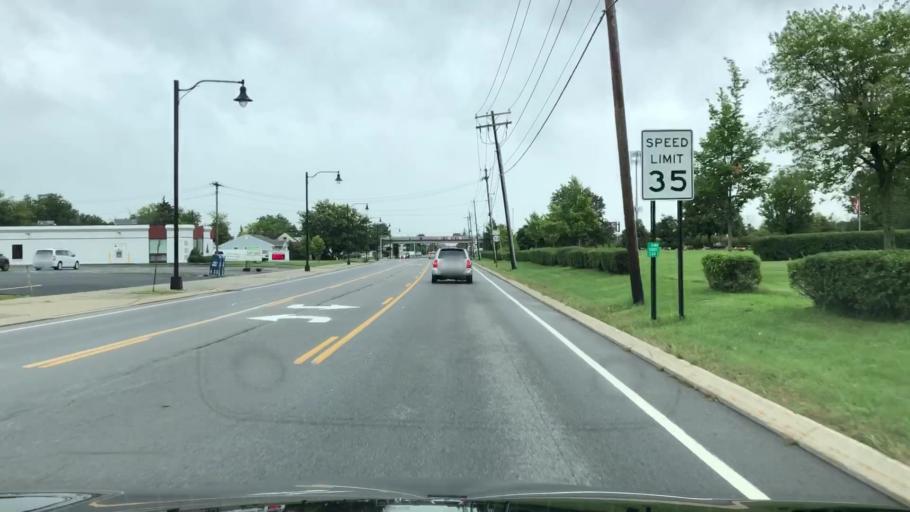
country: US
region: New York
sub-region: Erie County
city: Eggertsville
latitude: 42.9355
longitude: -78.7842
